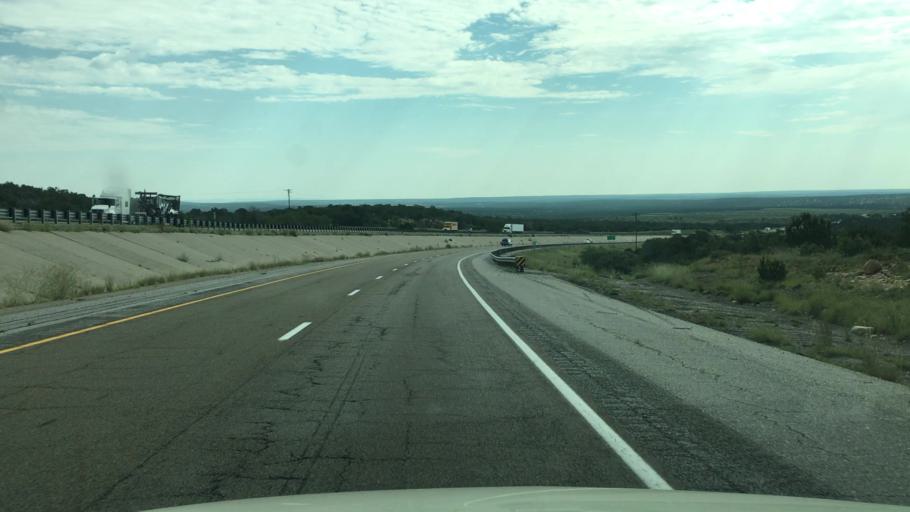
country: US
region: New Mexico
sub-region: Torrance County
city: Moriarty
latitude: 35.0044
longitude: -105.5449
